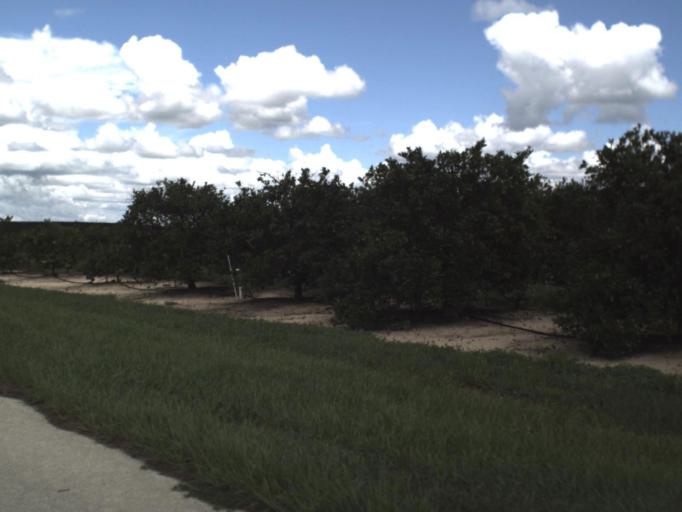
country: US
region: Florida
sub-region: Polk County
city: Fort Meade
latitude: 27.7450
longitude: -81.7279
